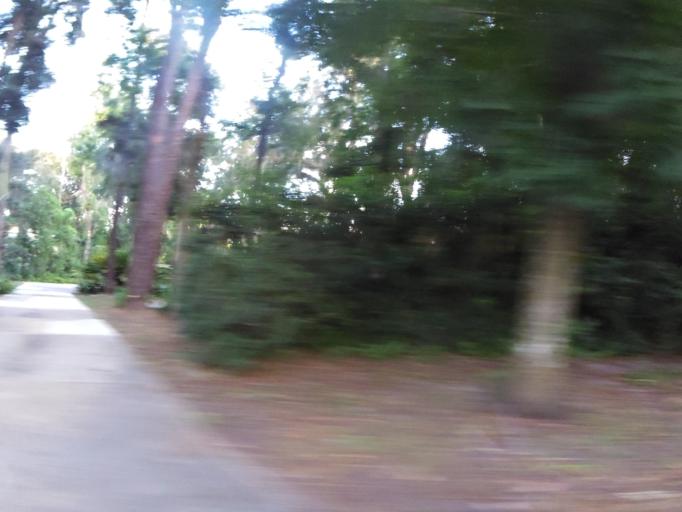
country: US
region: Florida
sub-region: Clay County
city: Orange Park
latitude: 30.2017
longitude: -81.6421
